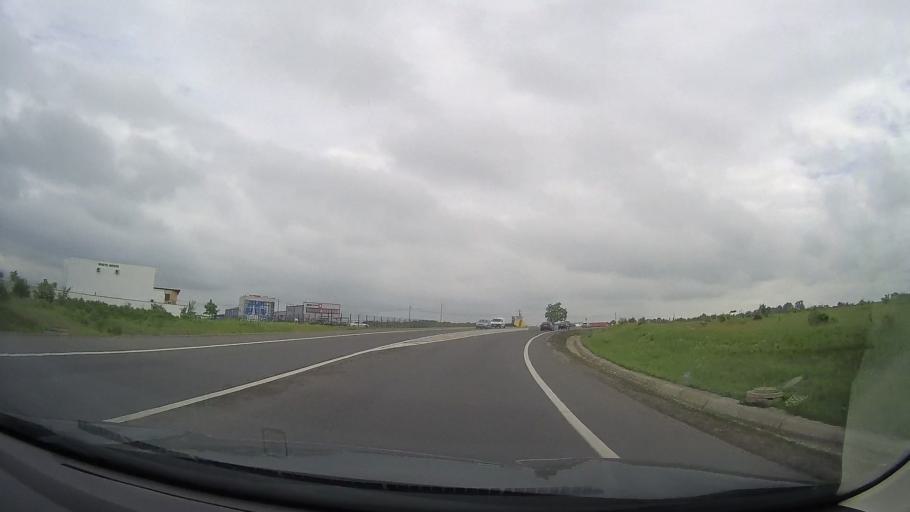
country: RO
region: Dolj
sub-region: Comuna Malu Mare
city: Preajba
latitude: 44.3222
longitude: 23.8650
